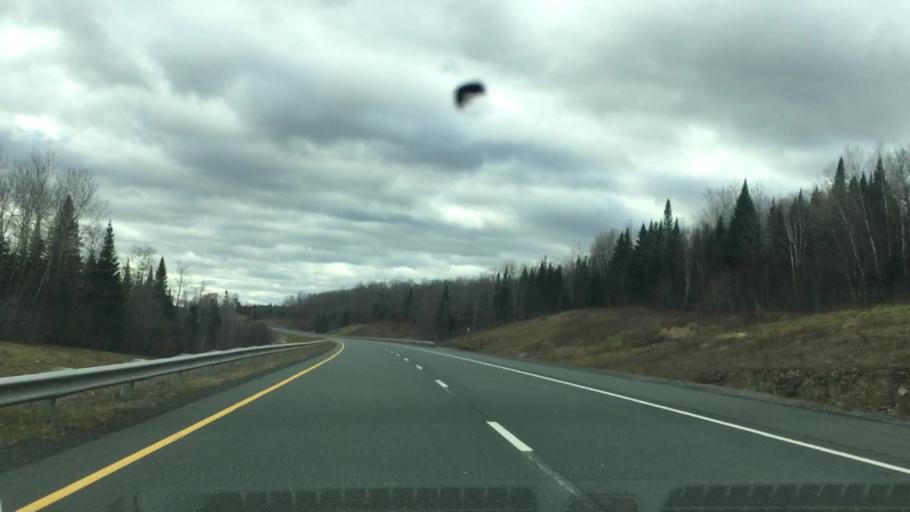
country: US
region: Maine
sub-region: Aroostook County
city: Fort Fairfield
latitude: 46.6499
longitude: -67.7416
